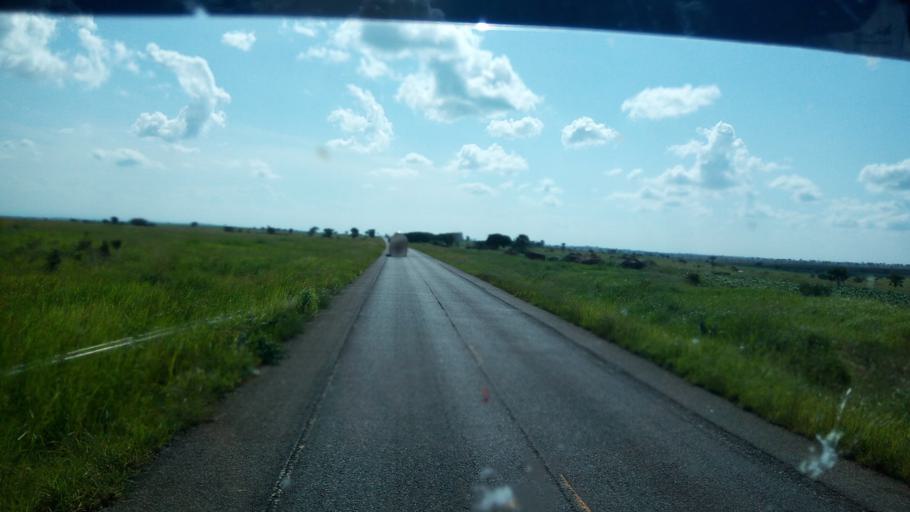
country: UG
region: Northern Region
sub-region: Nwoya District
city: Nwoya
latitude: 2.5593
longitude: 31.6944
